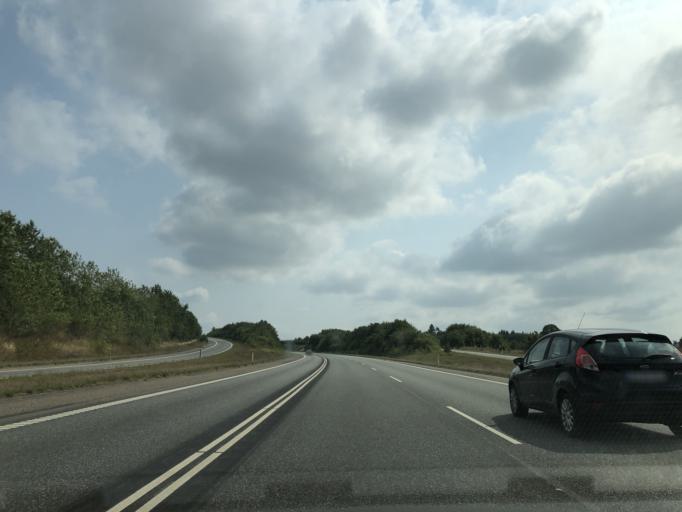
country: DK
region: Central Jutland
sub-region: Silkeborg Kommune
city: Kjellerup
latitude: 56.3436
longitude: 9.5331
